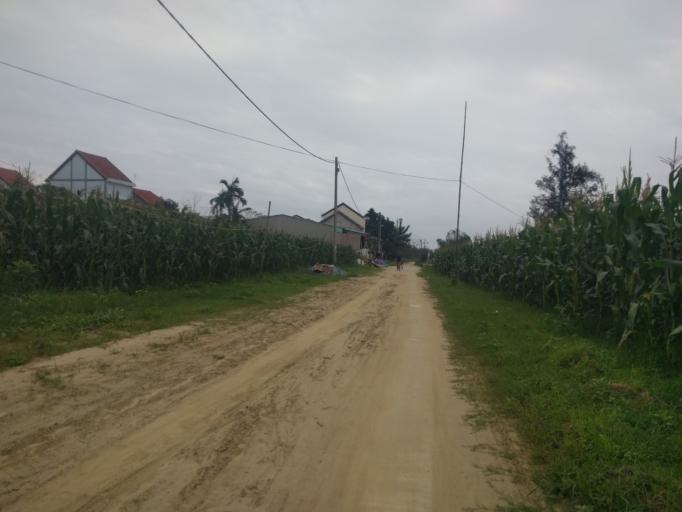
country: VN
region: Quang Nam
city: Hoi An
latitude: 15.8662
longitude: 108.3516
